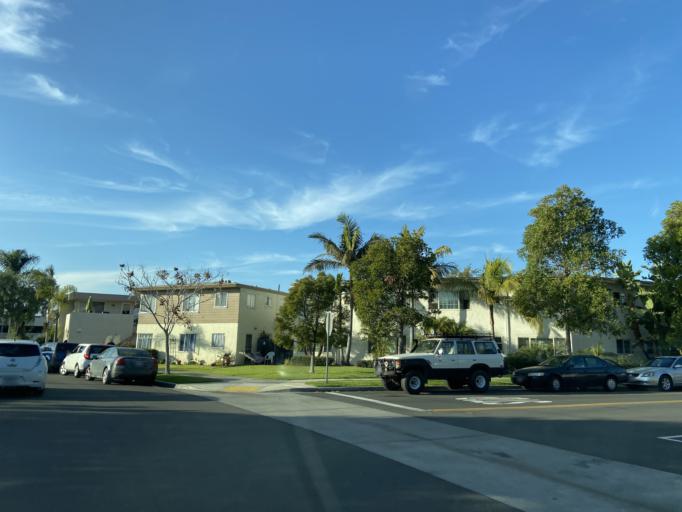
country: US
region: California
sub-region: San Diego County
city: Coronado
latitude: 32.6836
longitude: -117.1770
